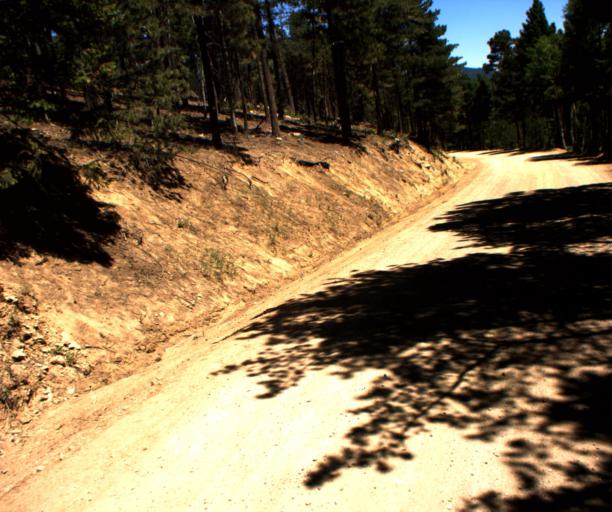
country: US
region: Arizona
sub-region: Graham County
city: Swift Trail Junction
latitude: 32.6874
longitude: -109.8993
